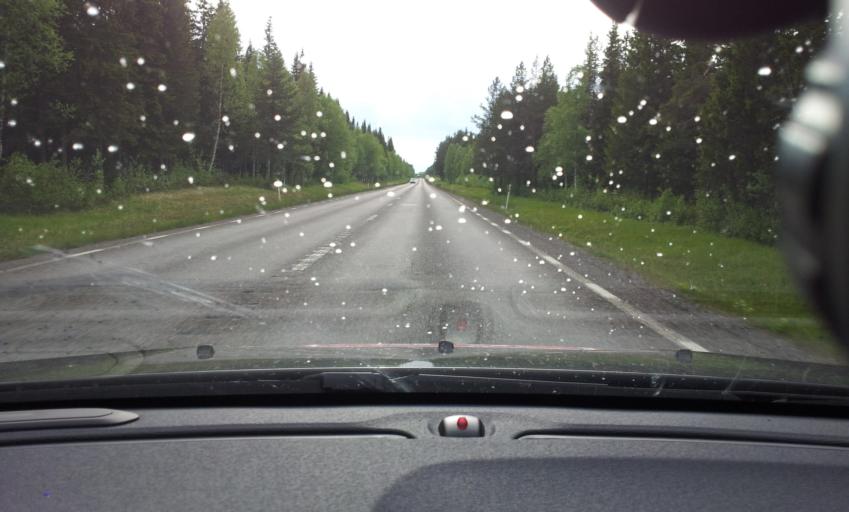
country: SE
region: Jaemtland
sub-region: OEstersunds Kommun
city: Lit
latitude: 63.2027
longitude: 14.9217
